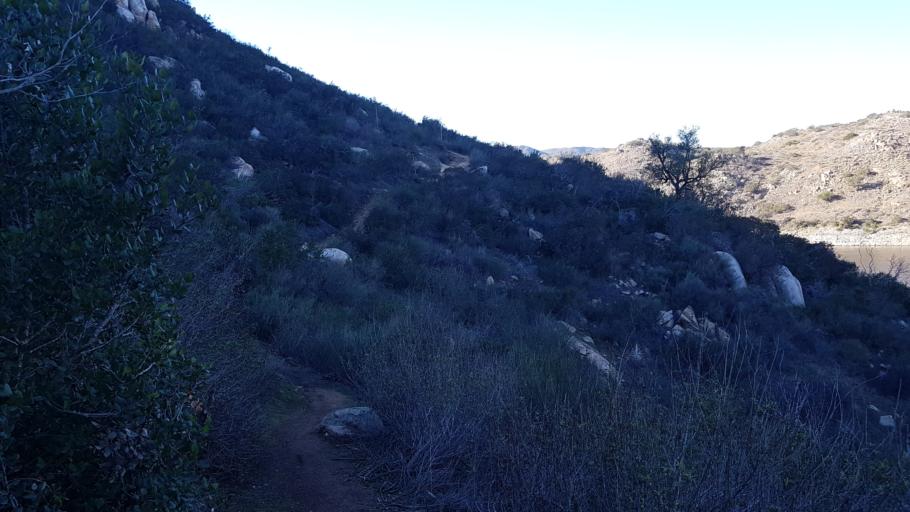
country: US
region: California
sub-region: San Diego County
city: Escondido
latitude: 33.0600
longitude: -117.1026
